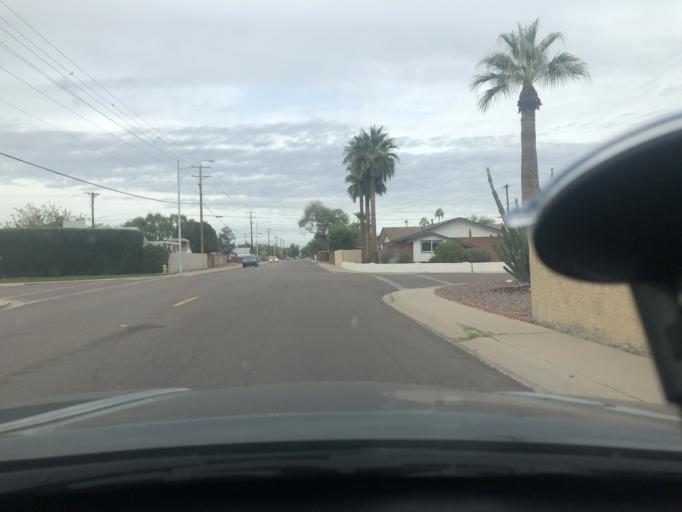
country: US
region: Arizona
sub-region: Maricopa County
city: Scottsdale
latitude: 33.4910
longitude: -111.9046
